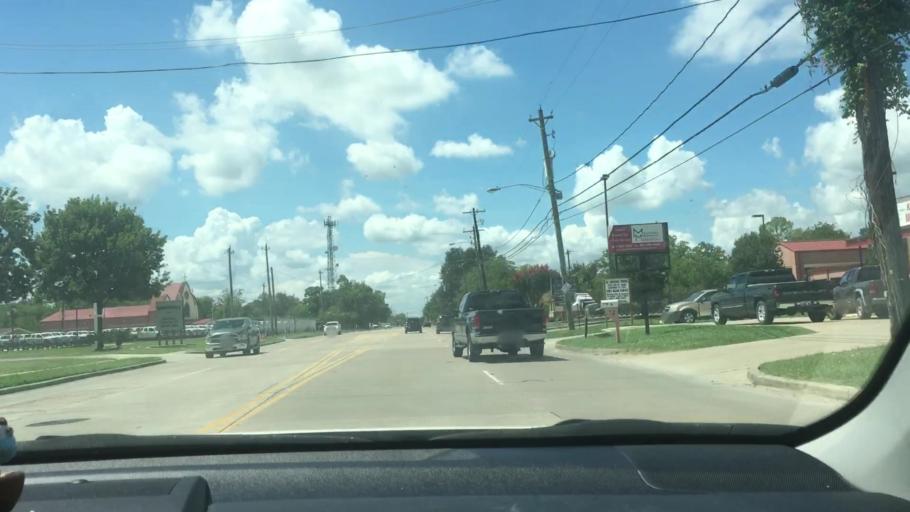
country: US
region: Texas
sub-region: Fort Bend County
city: Fifth Street
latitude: 29.5993
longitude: -95.5545
